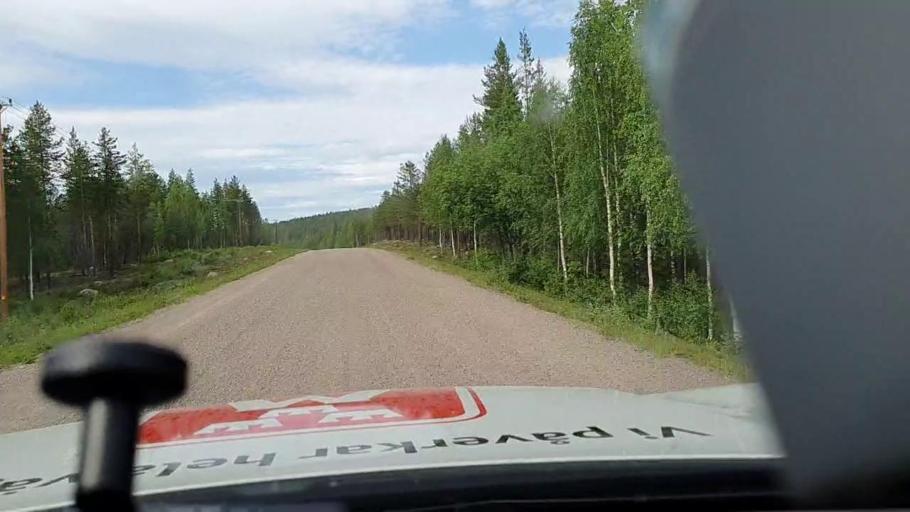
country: SE
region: Norrbotten
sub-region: Alvsbyns Kommun
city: AElvsbyn
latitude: 66.1240
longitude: 20.9943
